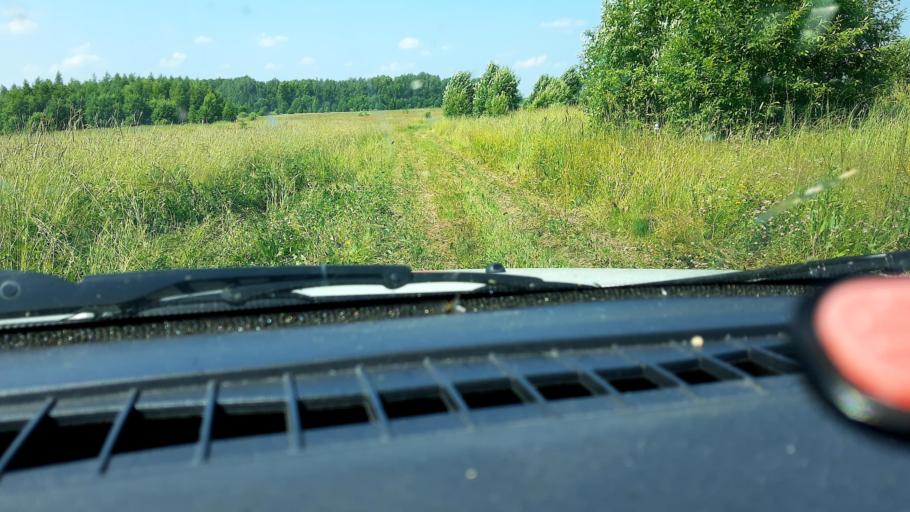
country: RU
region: Nizjnij Novgorod
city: Sharanga
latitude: 57.0458
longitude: 46.7311
